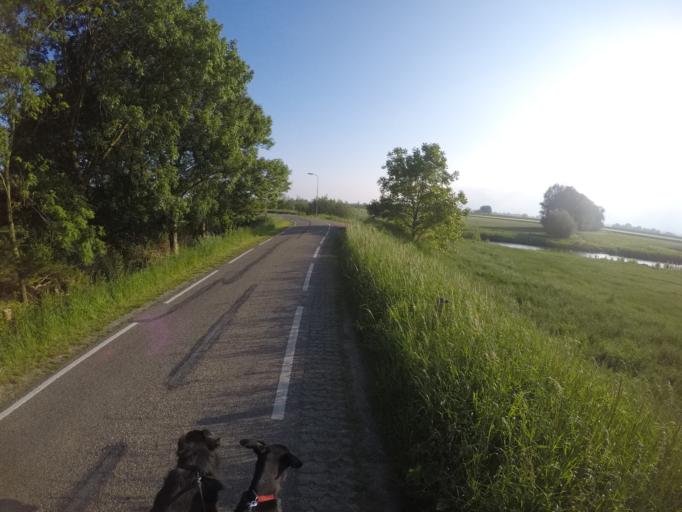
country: NL
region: Gelderland
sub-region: Gemeente Westervoort
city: Westervoort
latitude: 51.9550
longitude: 5.9640
